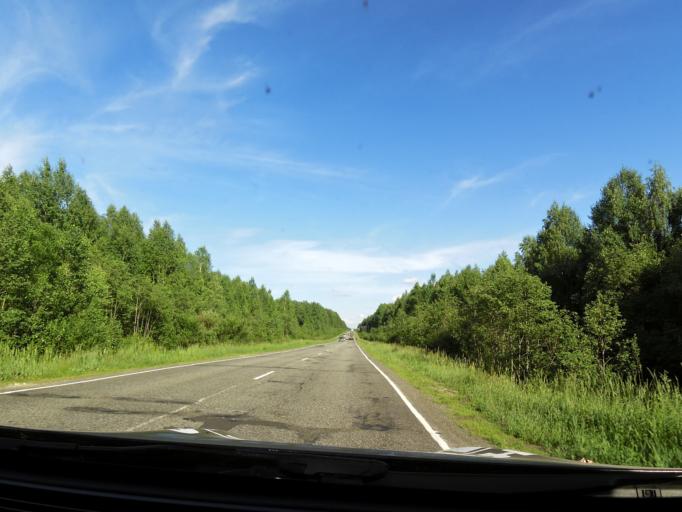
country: RU
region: Kirov
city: Belaya Kholunitsa
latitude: 58.9193
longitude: 51.1272
